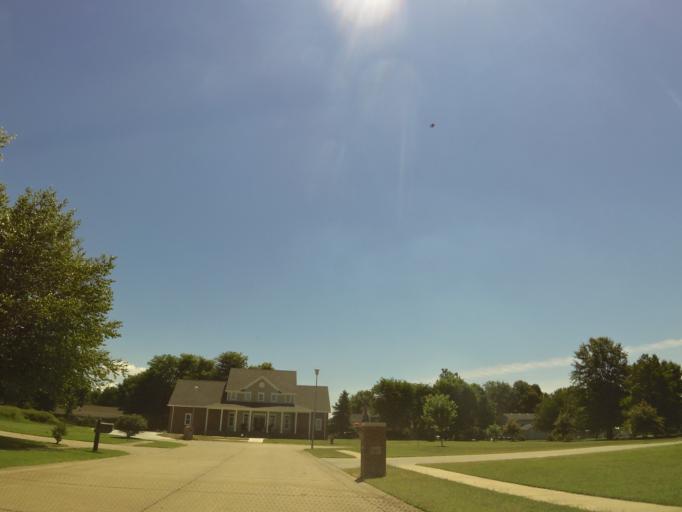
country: US
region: Missouri
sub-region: New Madrid County
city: New Madrid
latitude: 36.5995
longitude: -89.5249
